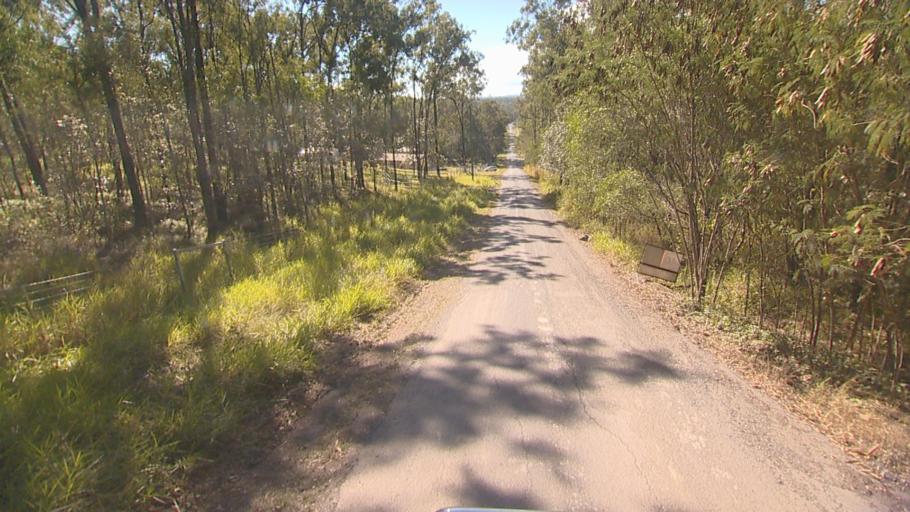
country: AU
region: Queensland
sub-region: Logan
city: Chambers Flat
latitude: -27.8115
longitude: 153.0817
